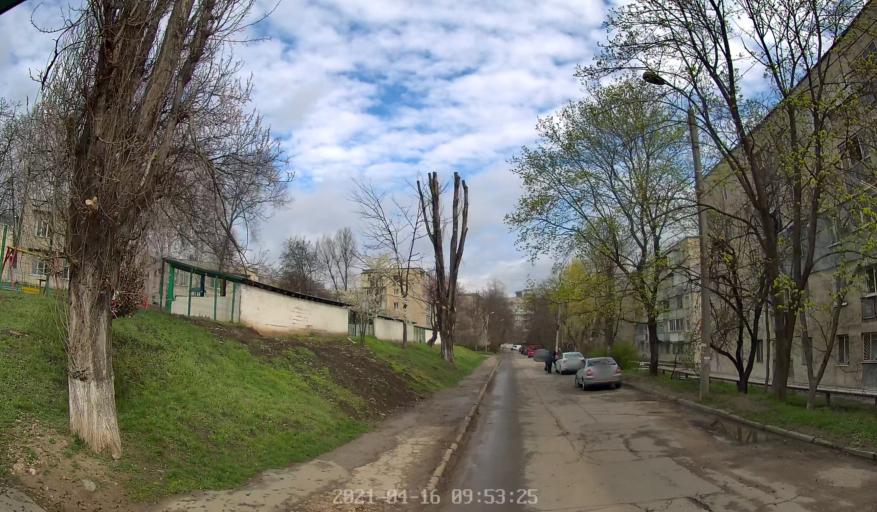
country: MD
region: Chisinau
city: Stauceni
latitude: 47.0589
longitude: 28.8445
